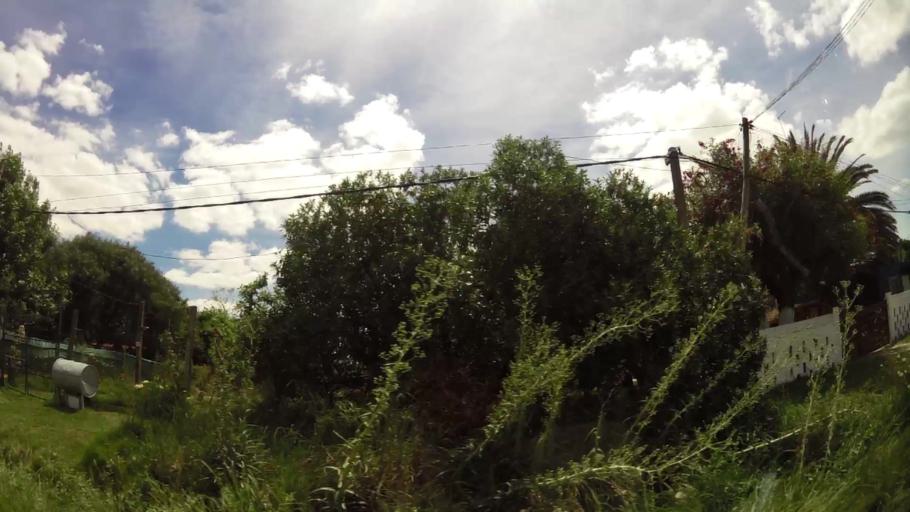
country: UY
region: San Jose
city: Delta del Tigre
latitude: -34.7512
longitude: -56.4231
